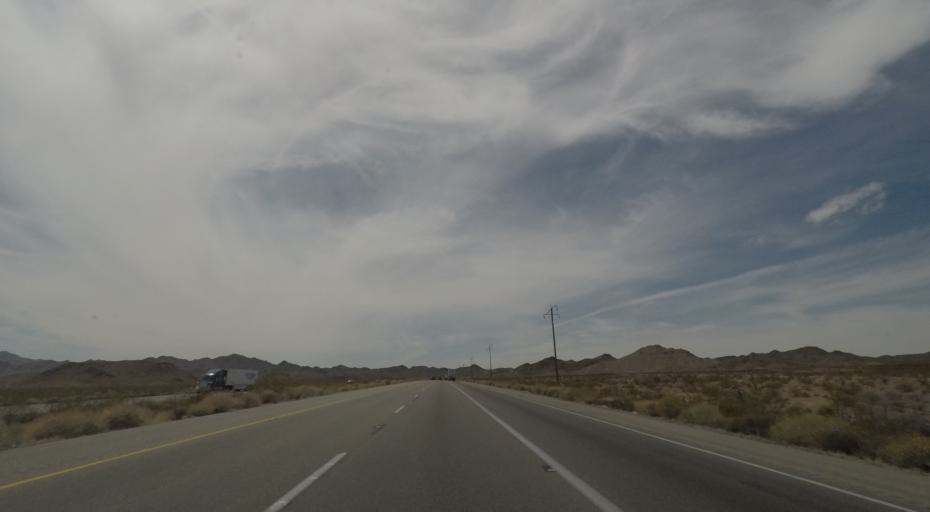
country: US
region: California
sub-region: San Bernardino County
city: Needles
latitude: 34.8326
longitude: -115.0158
